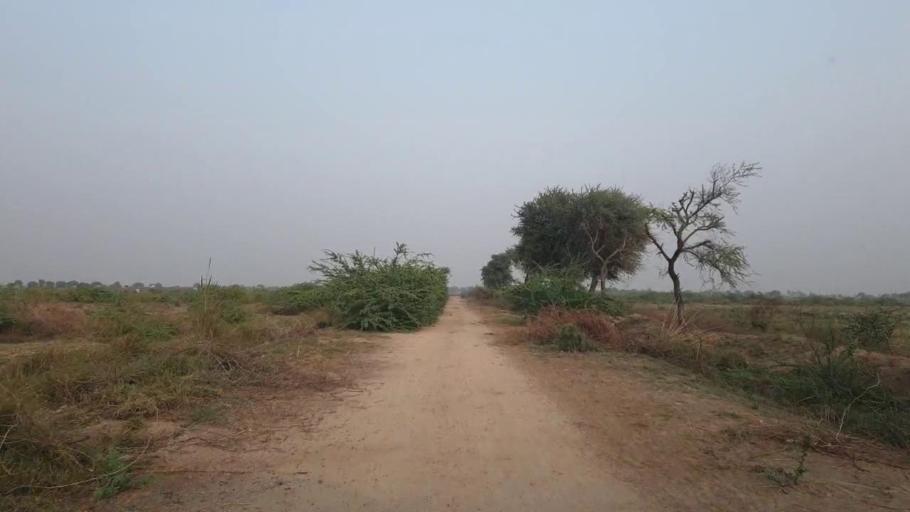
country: PK
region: Sindh
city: Mirpur Batoro
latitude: 24.6516
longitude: 68.3761
